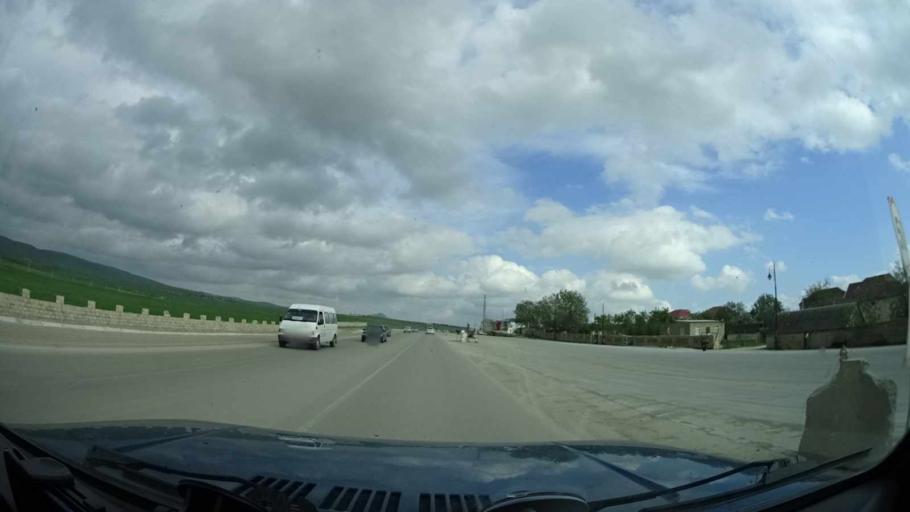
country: AZ
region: Samaxi
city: Shamakhi
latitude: 40.5900
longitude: 48.7085
